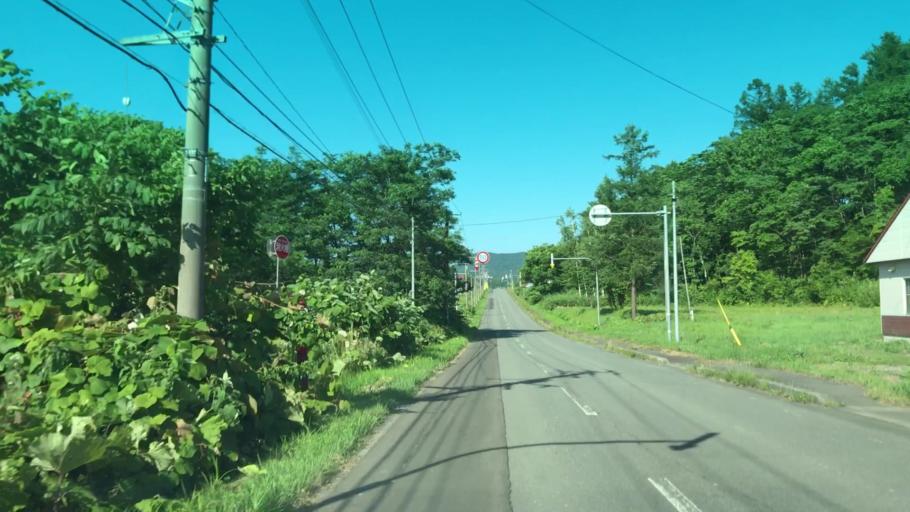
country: JP
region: Hokkaido
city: Yoichi
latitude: 43.0398
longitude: 140.7918
